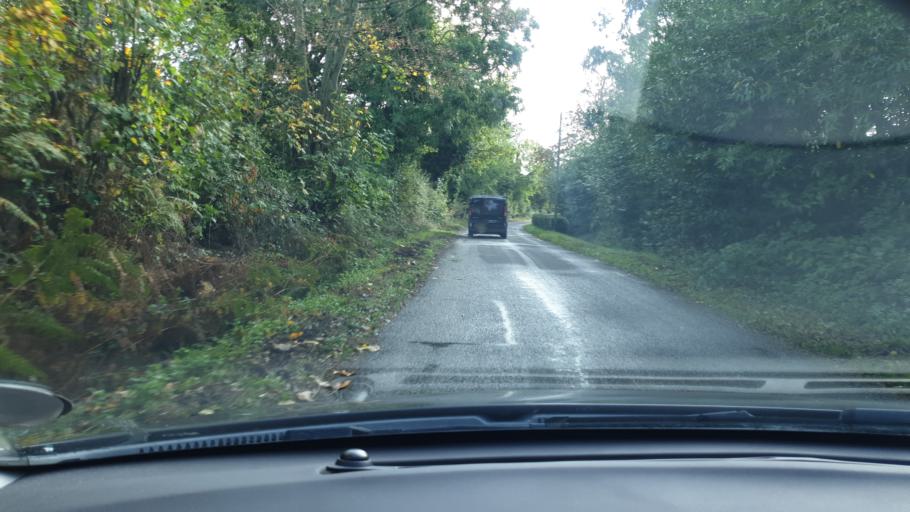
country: GB
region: England
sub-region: Essex
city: Alresford
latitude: 51.8584
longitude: 1.0270
